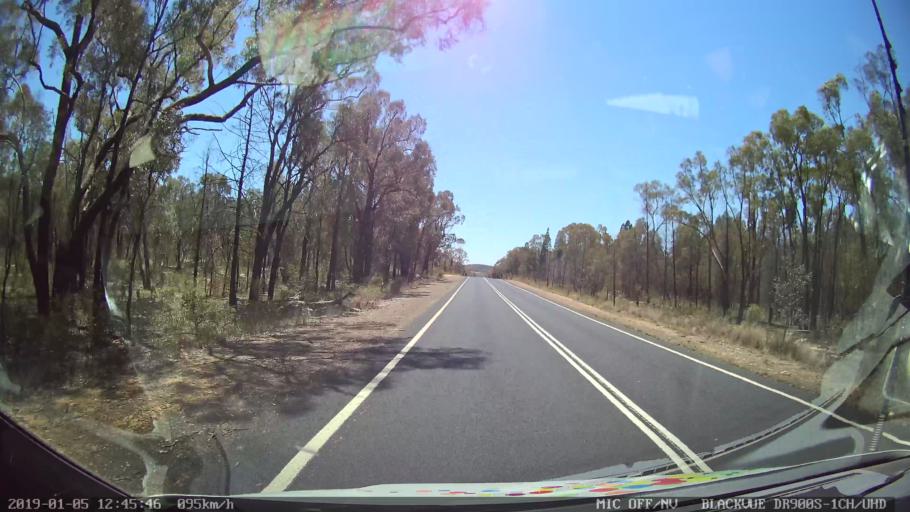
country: AU
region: New South Wales
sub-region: Warrumbungle Shire
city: Coonabarabran
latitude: -31.1247
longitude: 149.5540
